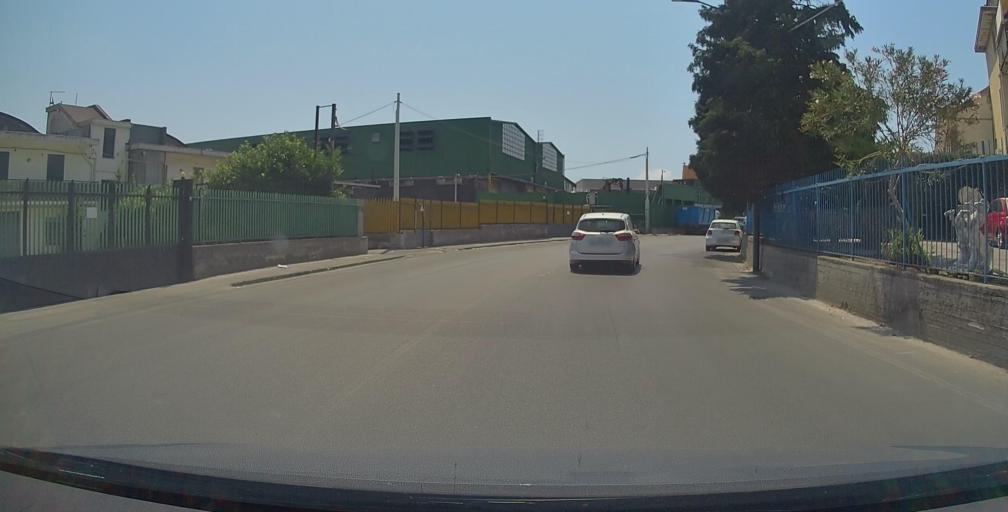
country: IT
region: Campania
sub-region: Provincia di Salerno
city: Cava De Tirreni
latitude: 40.7168
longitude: 14.6962
